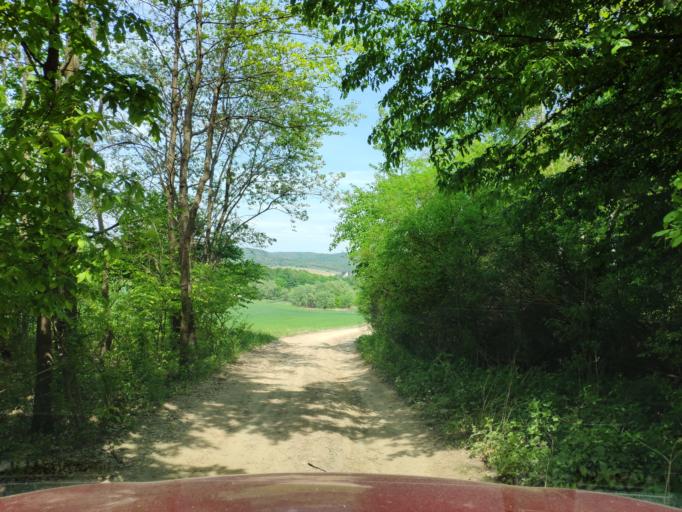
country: SK
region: Banskobystricky
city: Rimavska Sobota
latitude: 48.4732
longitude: 20.0811
